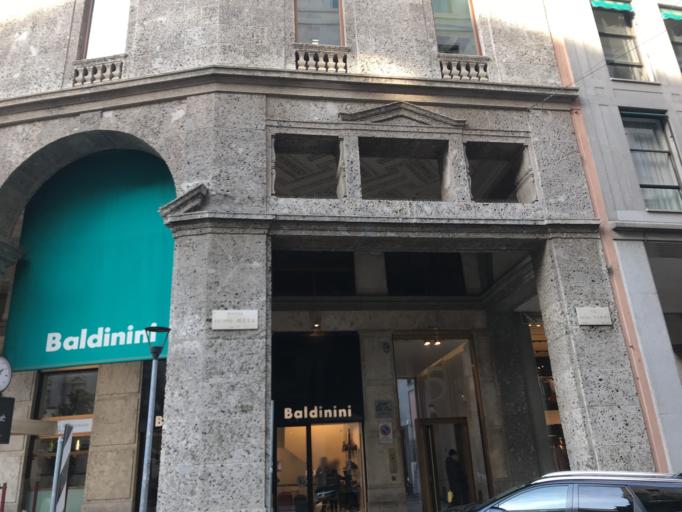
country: IT
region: Lombardy
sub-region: Citta metropolitana di Milano
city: Milano
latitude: 45.4671
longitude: 9.1938
